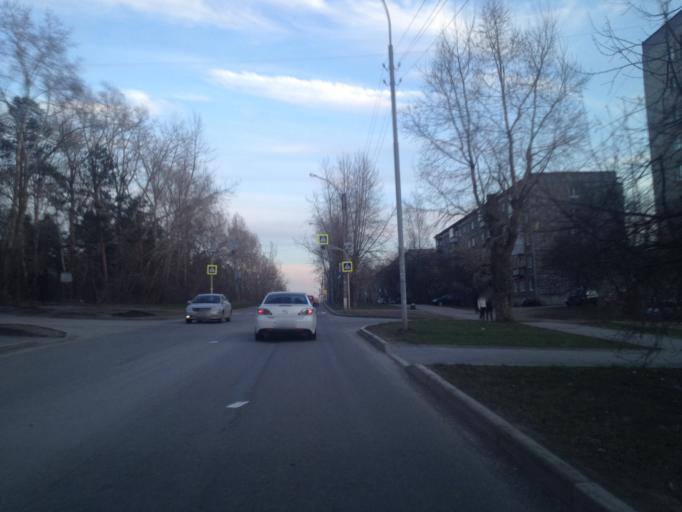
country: RU
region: Sverdlovsk
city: Sovkhoznyy
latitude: 56.7655
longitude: 60.6038
